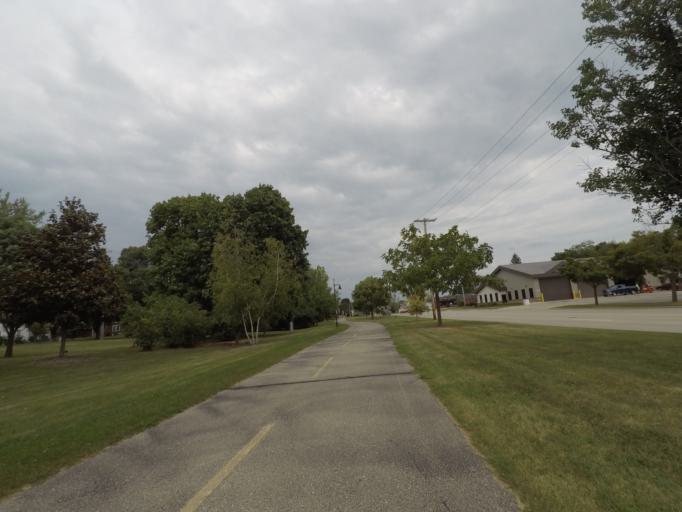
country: US
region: Wisconsin
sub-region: Jefferson County
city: Fort Atkinson
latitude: 42.9243
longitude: -88.8426
